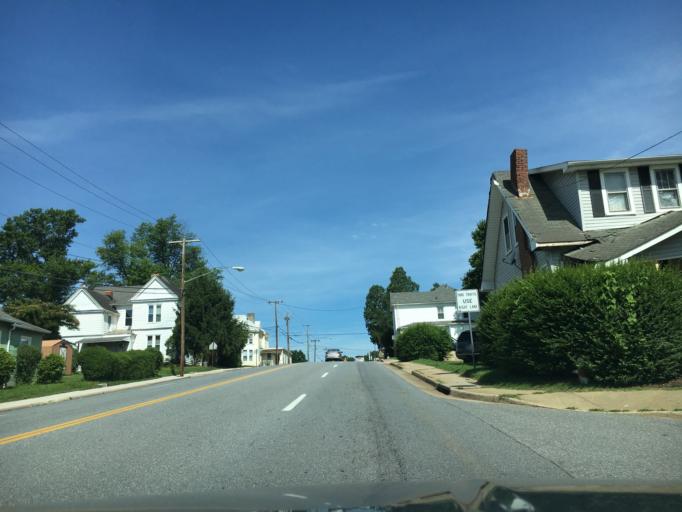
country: US
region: Virginia
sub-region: City of Lynchburg
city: West Lynchburg
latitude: 37.3970
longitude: -79.1680
